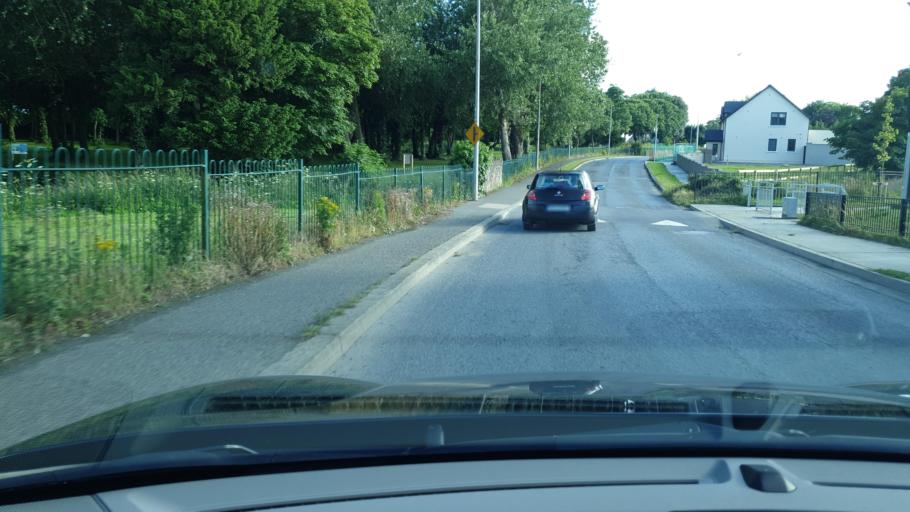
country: IE
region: Leinster
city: An Ros
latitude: 53.5250
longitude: -6.0980
